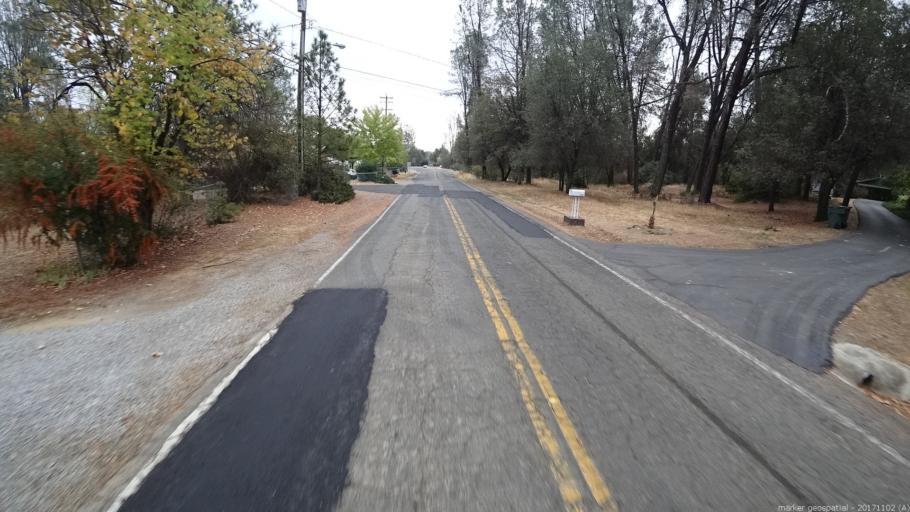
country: US
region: California
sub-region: Shasta County
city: Redding
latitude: 40.6329
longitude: -122.4073
